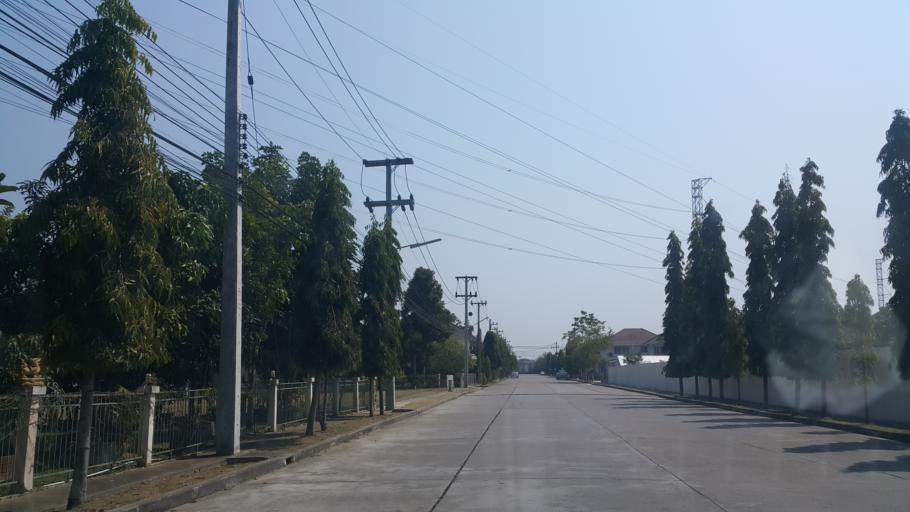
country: TH
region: Chiang Mai
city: Saraphi
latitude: 18.7343
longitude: 99.0743
